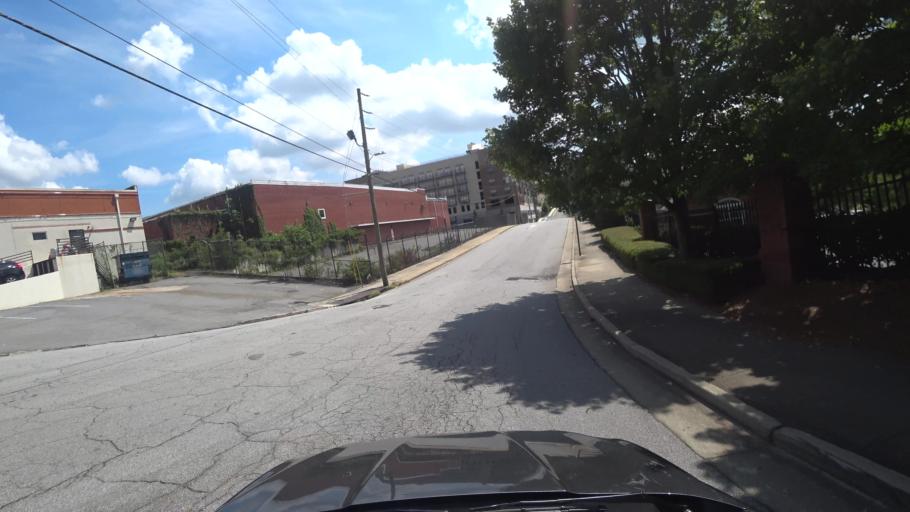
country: US
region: Georgia
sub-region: Fulton County
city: Atlanta
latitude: 33.8093
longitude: -84.4146
